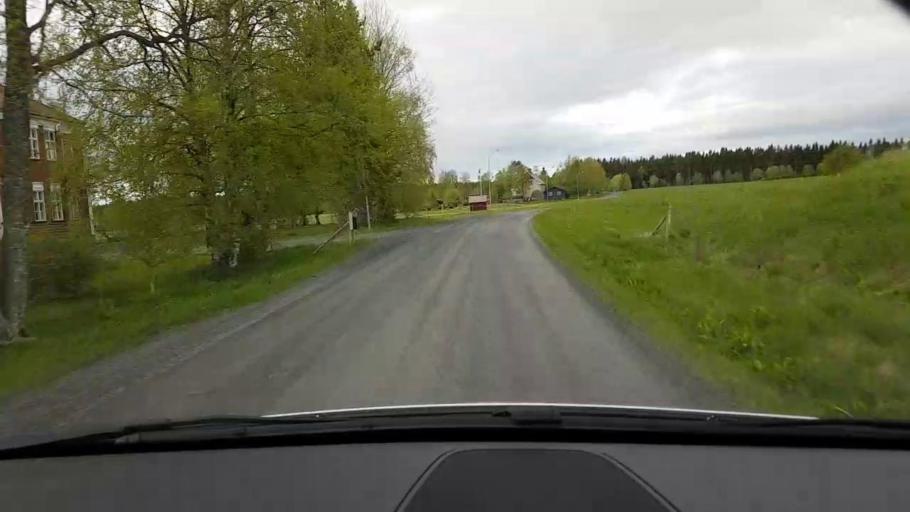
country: SE
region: Jaemtland
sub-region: Krokoms Kommun
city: Valla
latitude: 63.3058
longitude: 14.0065
